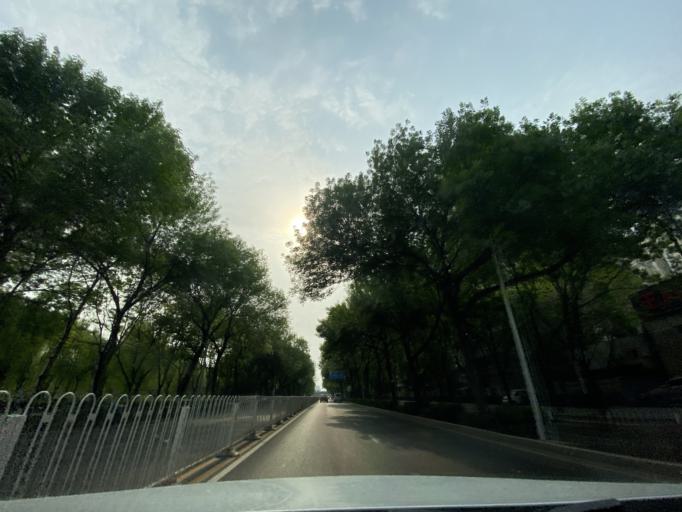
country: CN
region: Beijing
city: Qinghe
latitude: 39.9752
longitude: 116.3527
